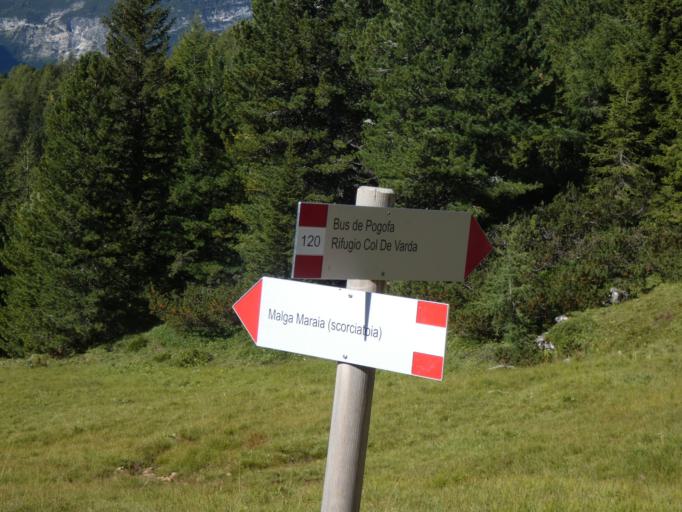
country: IT
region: Veneto
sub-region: Provincia di Belluno
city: San Vito
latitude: 46.5616
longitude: 12.2902
